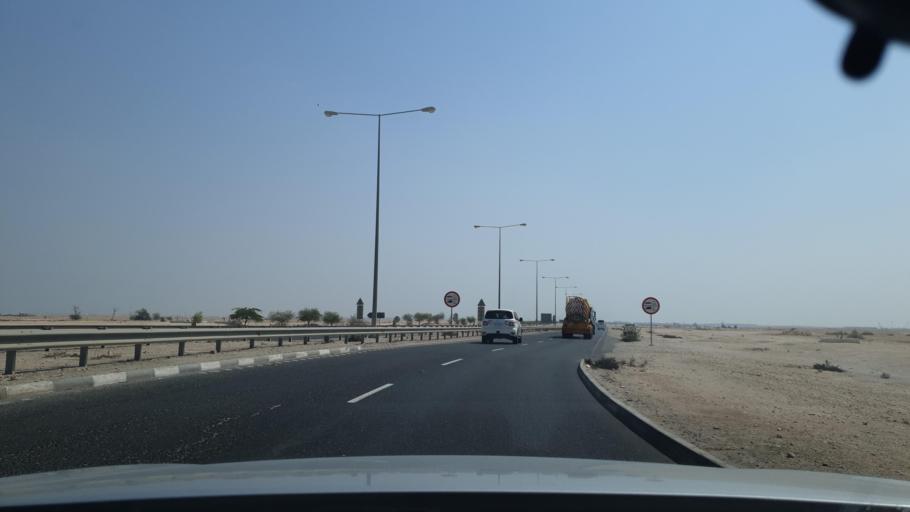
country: QA
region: Al Khawr
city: Al Khawr
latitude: 25.7535
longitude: 51.4759
